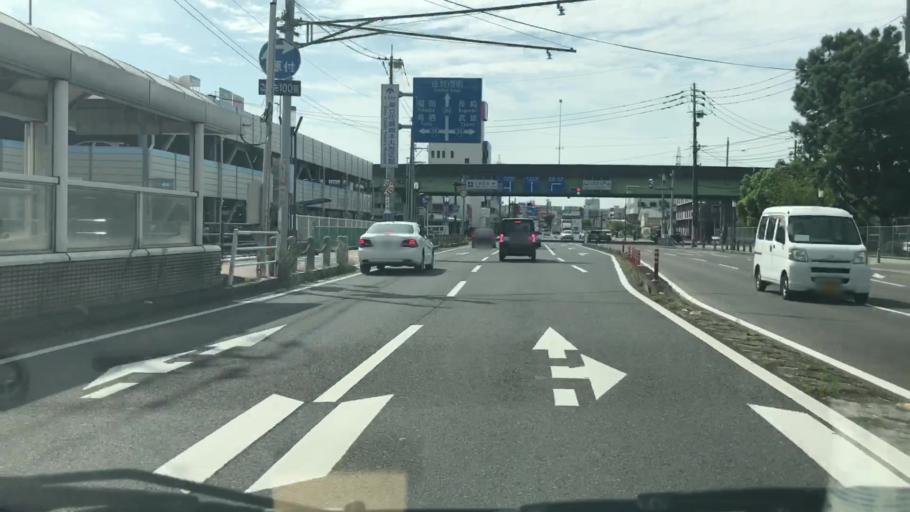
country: JP
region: Saga Prefecture
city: Saga-shi
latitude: 33.2753
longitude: 130.2935
